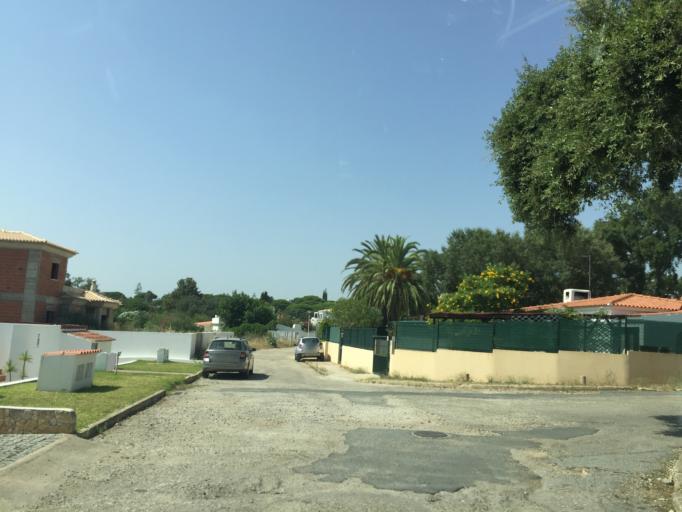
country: PT
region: Faro
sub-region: Albufeira
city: Ferreiras
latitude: 37.1042
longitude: -8.2032
